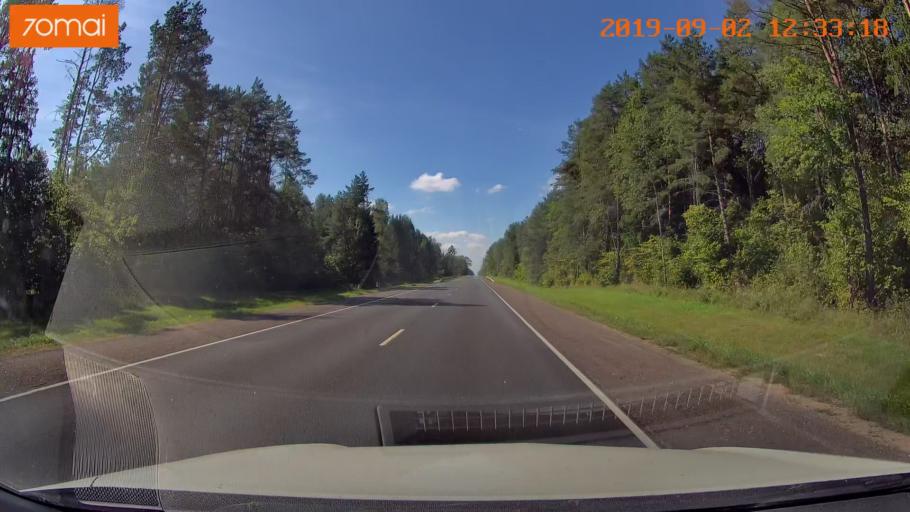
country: RU
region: Smolensk
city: Shumyachi
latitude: 53.8189
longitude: 32.4319
